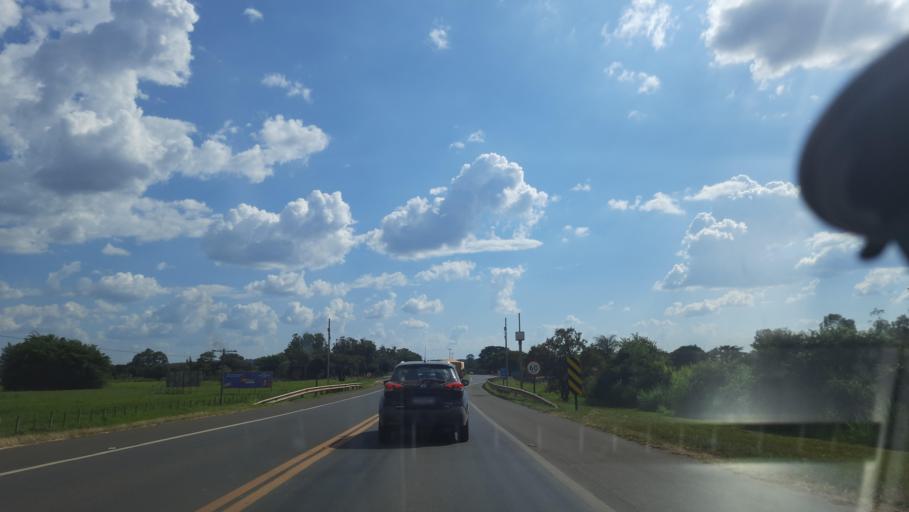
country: BR
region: Sao Paulo
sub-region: Casa Branca
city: Casa Branca
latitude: -21.7407
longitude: -46.9781
